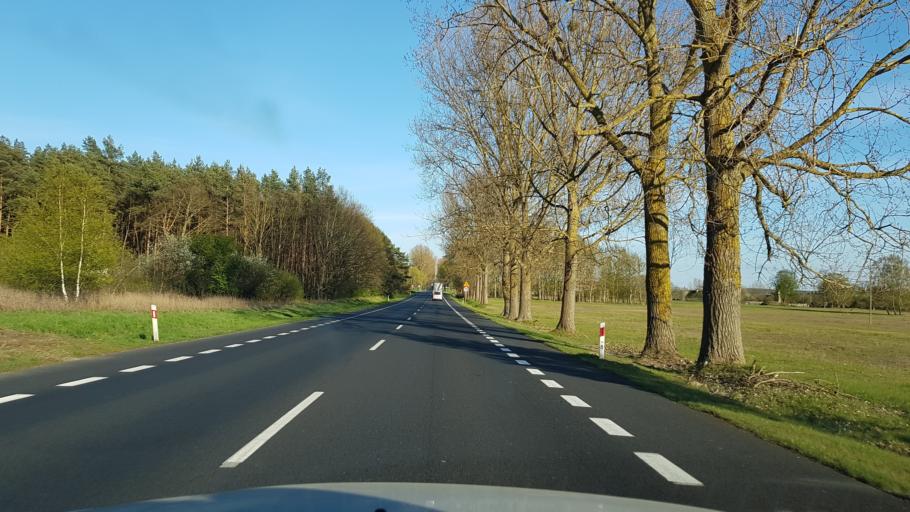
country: PL
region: West Pomeranian Voivodeship
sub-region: Powiat kamienski
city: Wolin
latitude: 53.8568
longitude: 14.5768
